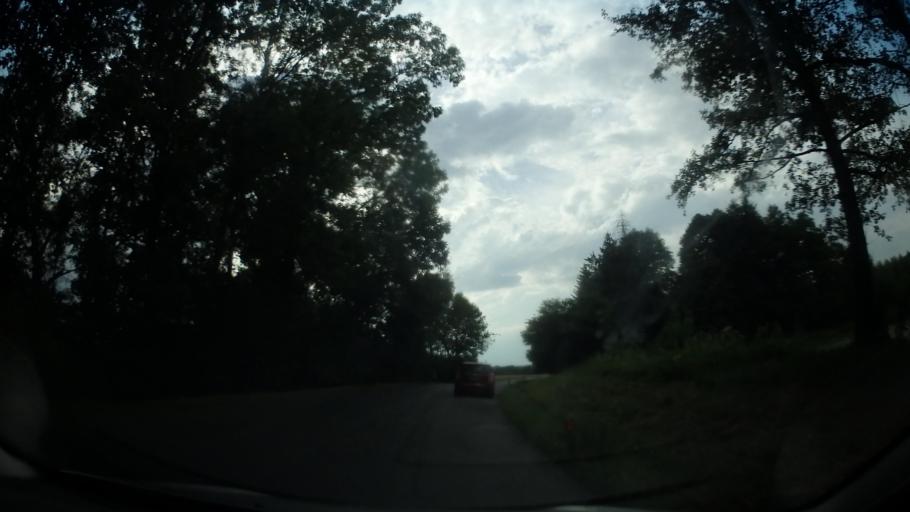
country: CZ
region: Pardubicky
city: Ronov nad Doubravou
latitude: 49.8835
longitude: 15.5519
